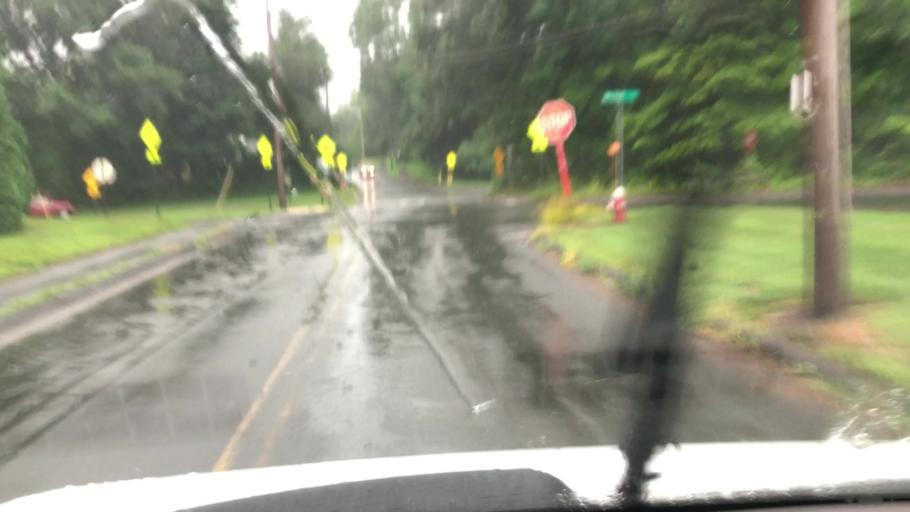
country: US
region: Massachusetts
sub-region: Hampshire County
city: Northampton
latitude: 42.3352
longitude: -72.6535
